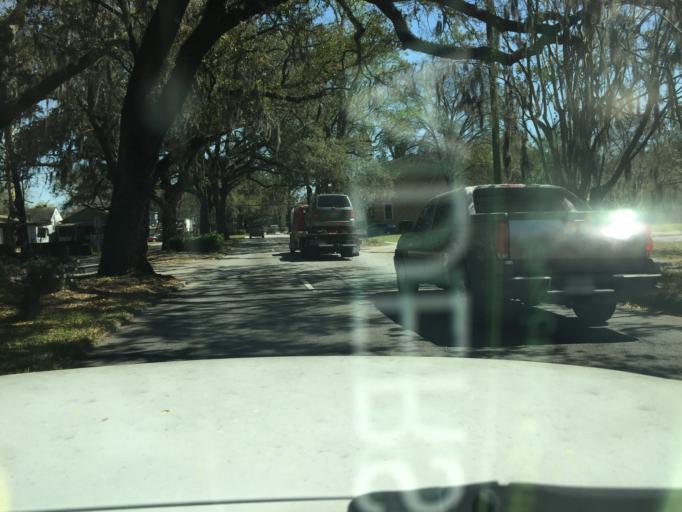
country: US
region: Georgia
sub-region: Chatham County
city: Savannah
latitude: 32.0598
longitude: -81.1104
